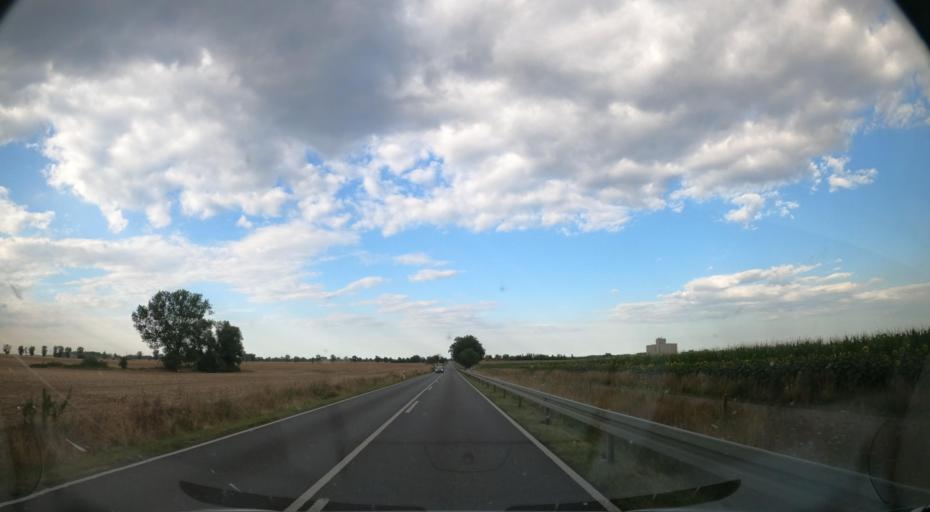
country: DE
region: Mecklenburg-Vorpommern
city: Pasewalk
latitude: 53.5076
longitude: 13.9634
